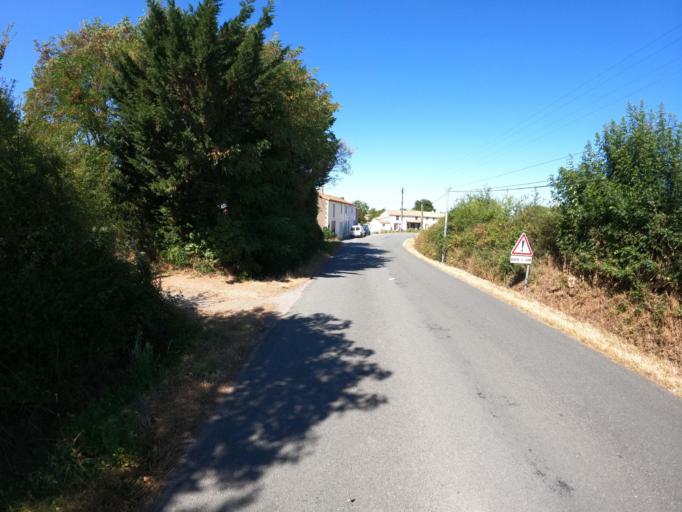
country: FR
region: Pays de la Loire
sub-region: Departement de la Vendee
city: Saint-Aubin-des-Ormeaux
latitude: 46.9972
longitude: -1.0311
